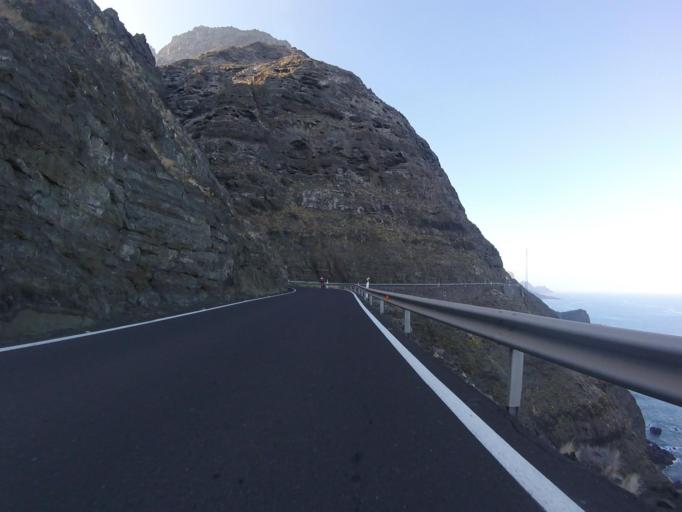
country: ES
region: Canary Islands
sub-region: Provincia de Las Palmas
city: Agaete
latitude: 28.0699
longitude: -15.7195
